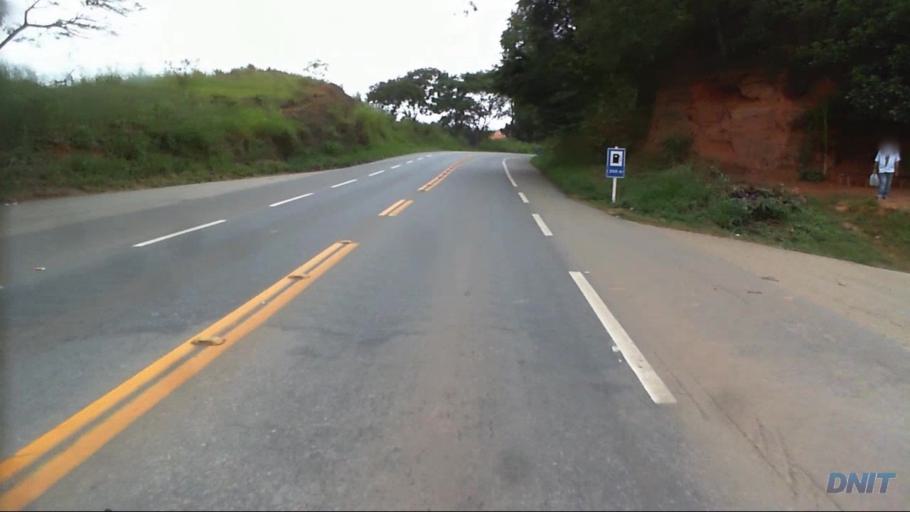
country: BR
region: Minas Gerais
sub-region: Nova Era
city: Nova Era
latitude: -19.7442
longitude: -43.0219
